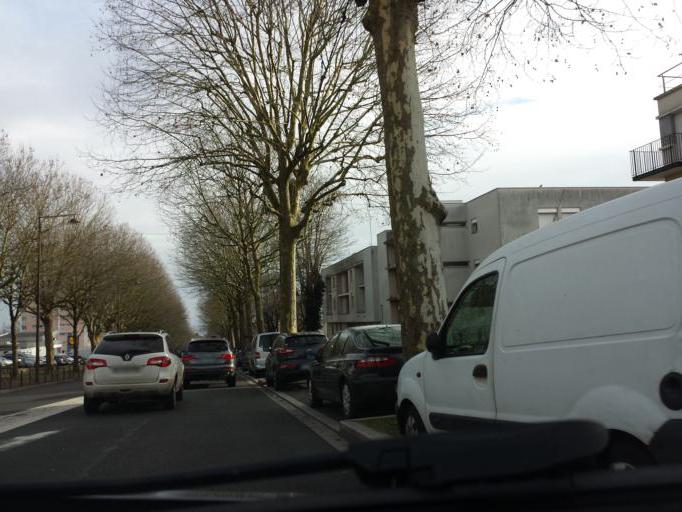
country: FR
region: Ile-de-France
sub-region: Departement des Hauts-de-Seine
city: Chatenay-Malabry
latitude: 48.7652
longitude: 2.2625
